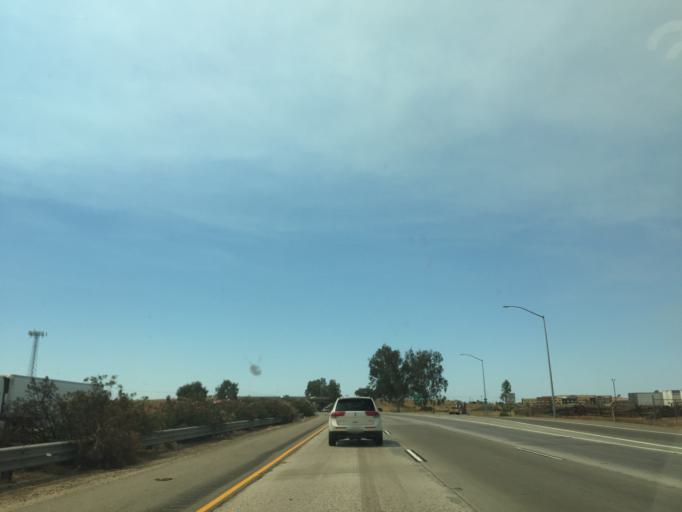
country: US
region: California
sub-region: Kern County
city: Oildale
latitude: 35.4322
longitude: -119.0734
